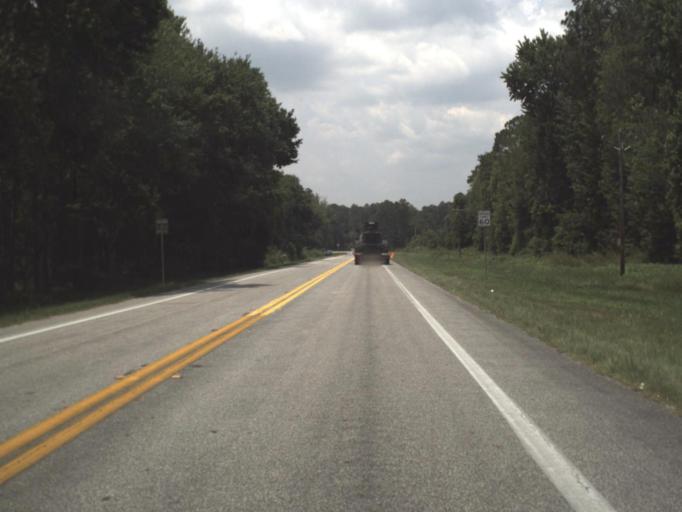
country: US
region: Florida
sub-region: Putnam County
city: Palatka
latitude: 29.6181
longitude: -81.7054
